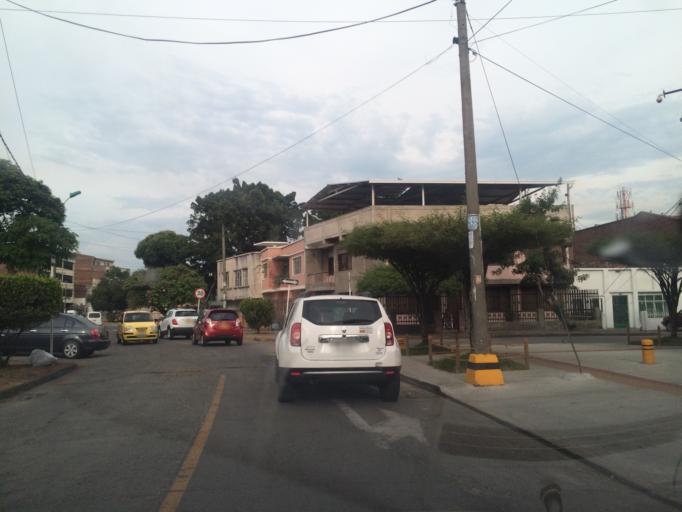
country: CO
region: Valle del Cauca
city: Cali
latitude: 3.4326
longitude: -76.5350
